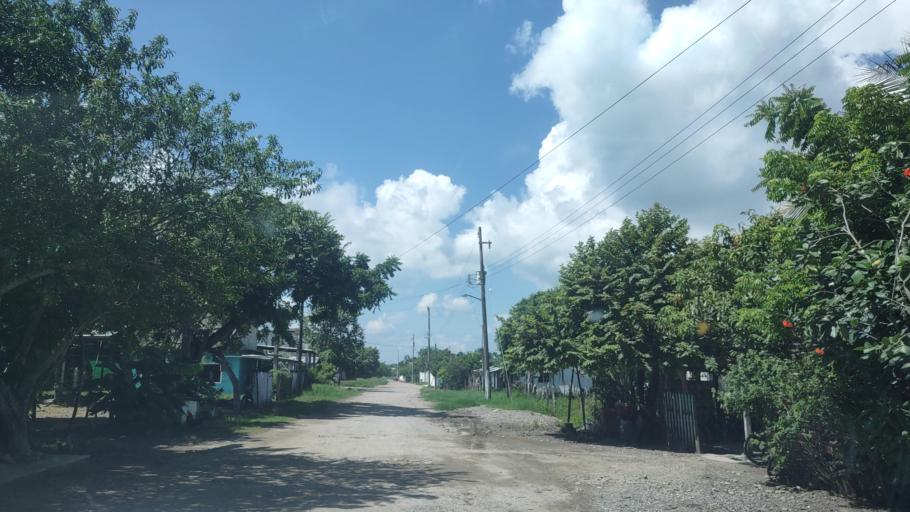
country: MX
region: Veracruz
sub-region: Ozuluama de Mascarenas
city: Cucharas
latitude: 21.6189
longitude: -97.6550
